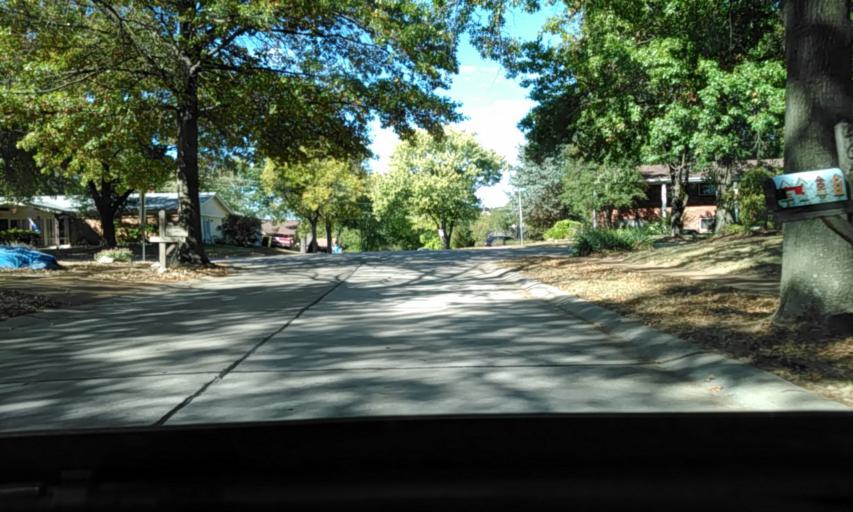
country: US
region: Missouri
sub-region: Jefferson County
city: Arnold
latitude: 38.4780
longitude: -90.3731
